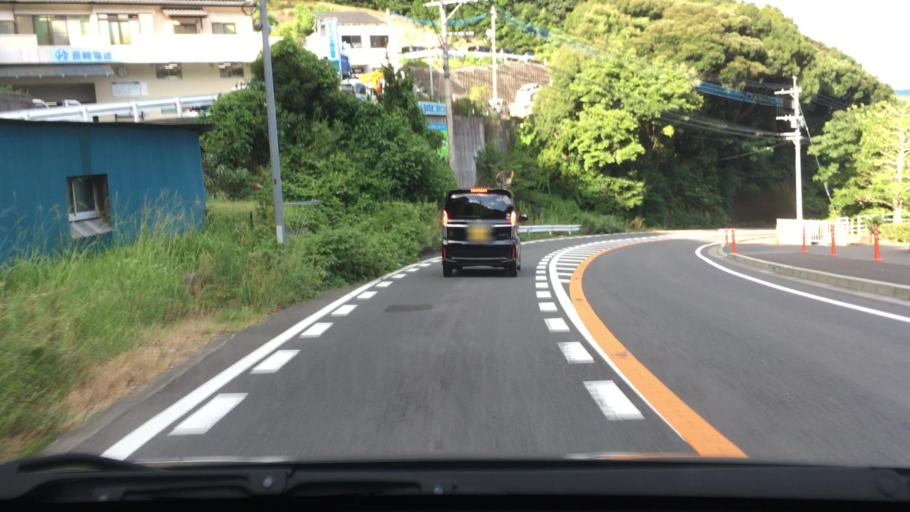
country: JP
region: Nagasaki
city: Togitsu
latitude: 32.8101
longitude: 129.8163
